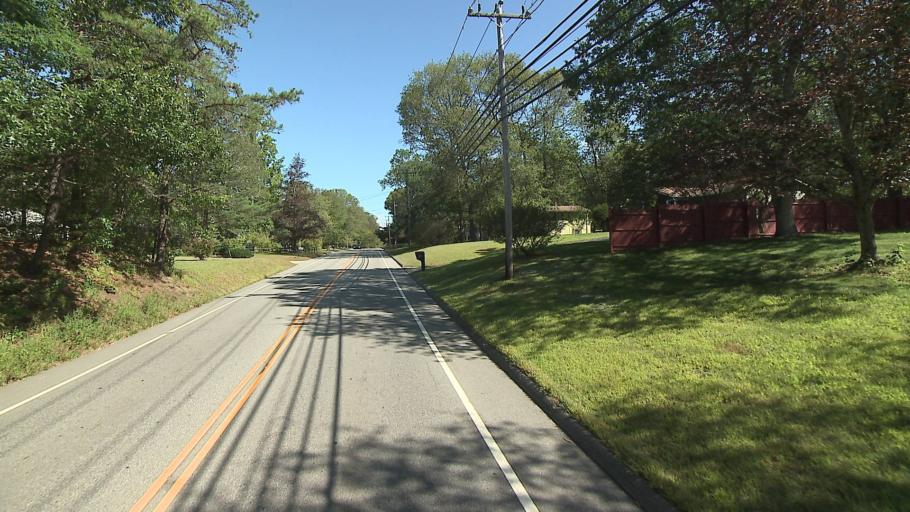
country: US
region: Connecticut
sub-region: Windham County
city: East Brooklyn
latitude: 41.7707
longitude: -71.8979
